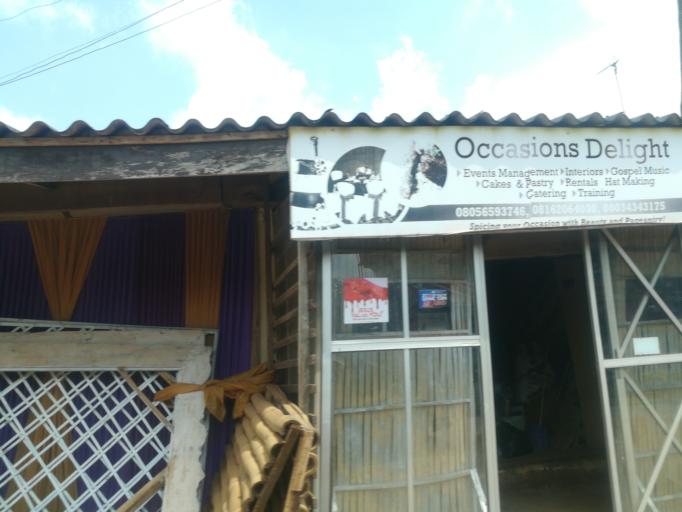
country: NG
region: Oyo
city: Ibadan
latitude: 7.4350
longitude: 3.9424
